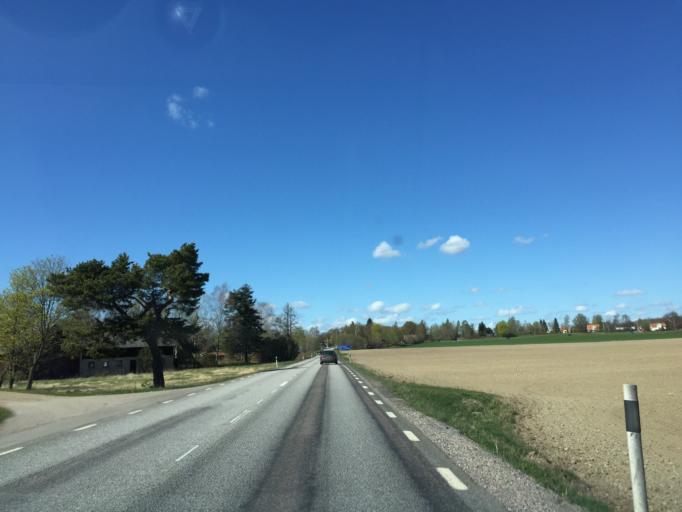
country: SE
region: OErebro
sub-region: Hallsbergs Kommun
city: Skollersta
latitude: 59.1248
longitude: 15.3283
